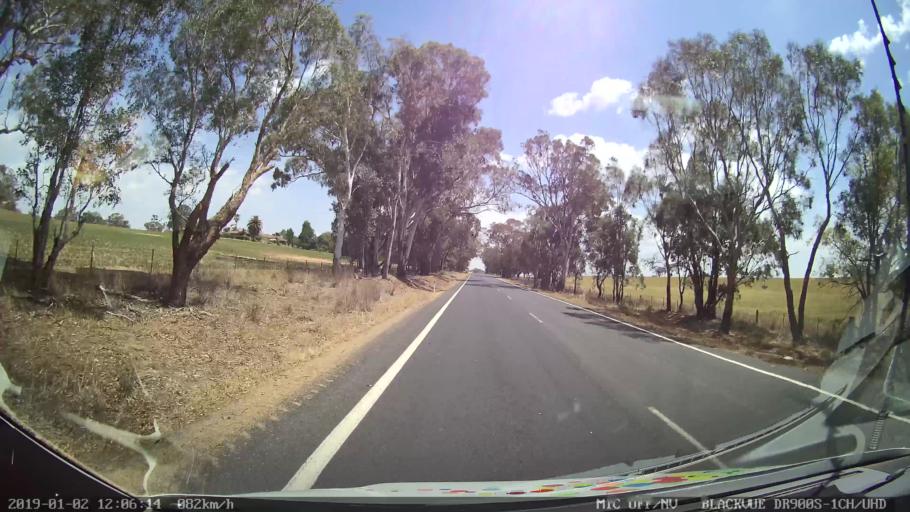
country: AU
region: New South Wales
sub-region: Young
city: Young
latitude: -34.5052
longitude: 148.2961
